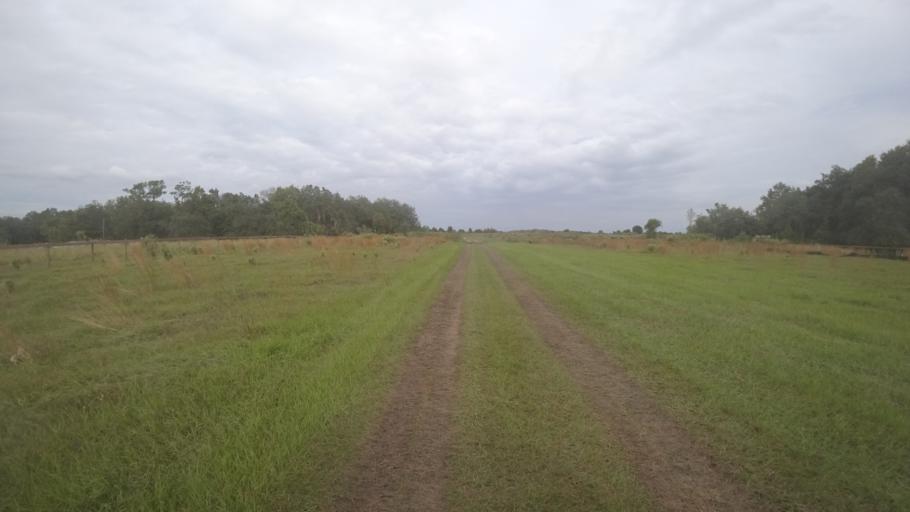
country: US
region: Florida
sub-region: Sarasota County
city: Lake Sarasota
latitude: 27.2908
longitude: -82.2149
